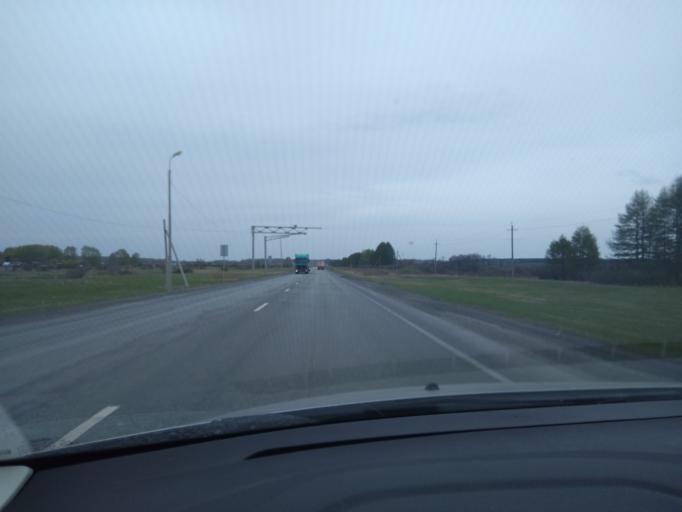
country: RU
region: Sverdlovsk
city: Troitskiy
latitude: 57.0767
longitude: 63.6209
